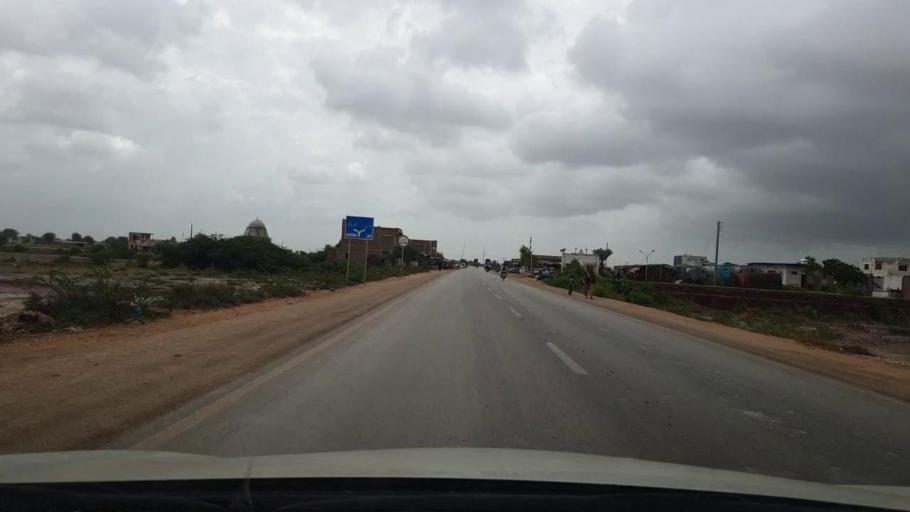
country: PK
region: Sindh
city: Mirpur Batoro
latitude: 24.6438
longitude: 68.4107
